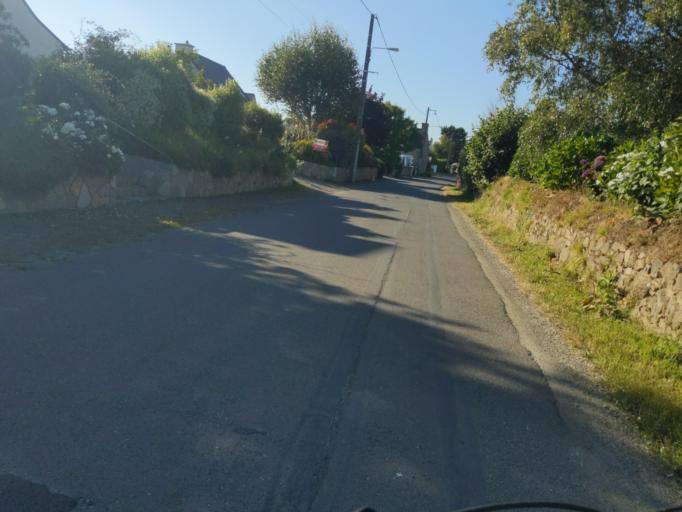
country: FR
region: Brittany
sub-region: Departement des Cotes-d'Armor
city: Pleubian
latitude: 48.8481
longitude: -3.1381
